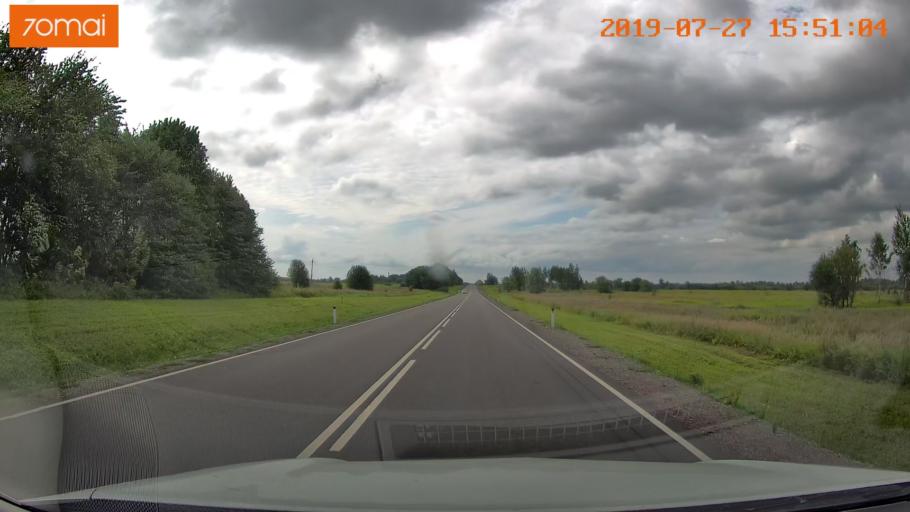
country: RU
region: Kaliningrad
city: Chernyakhovsk
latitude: 54.6021
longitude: 21.9902
